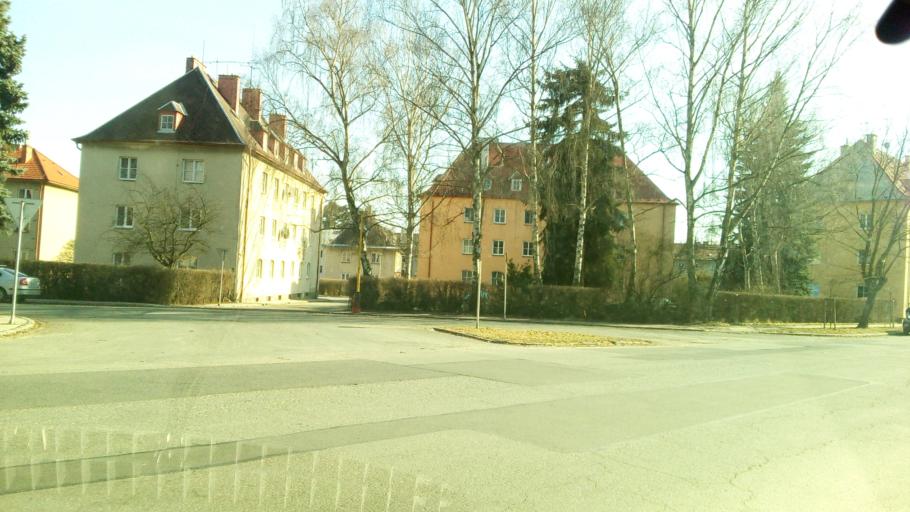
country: CZ
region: Olomoucky
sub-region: Okres Sumperk
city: Sumperk
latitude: 49.9626
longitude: 16.9645
